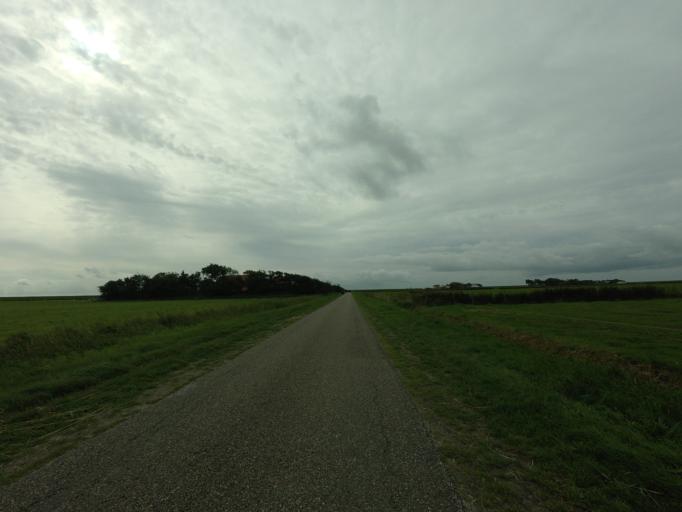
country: NL
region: Friesland
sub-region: Gemeente Ameland
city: Nes
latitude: 53.4384
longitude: 5.7071
